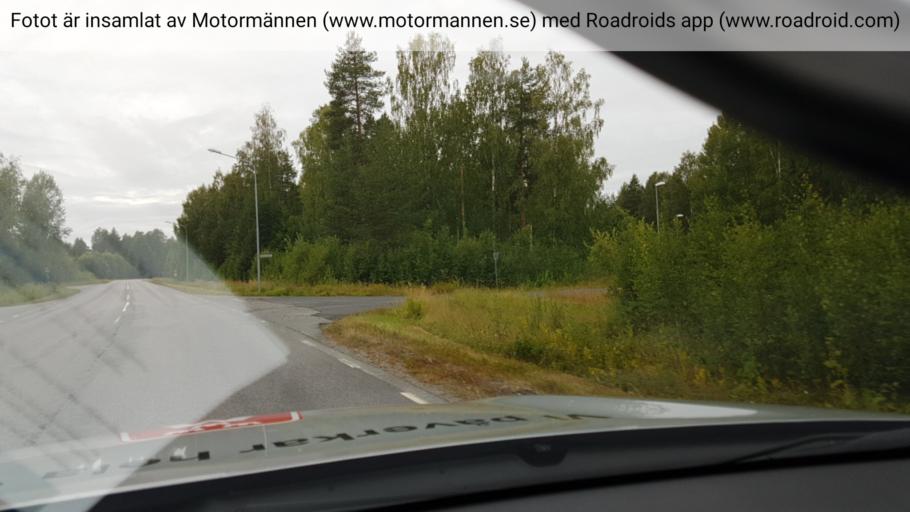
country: SE
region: Norrbotten
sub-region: Bodens Kommun
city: Boden
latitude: 65.8158
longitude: 21.6352
